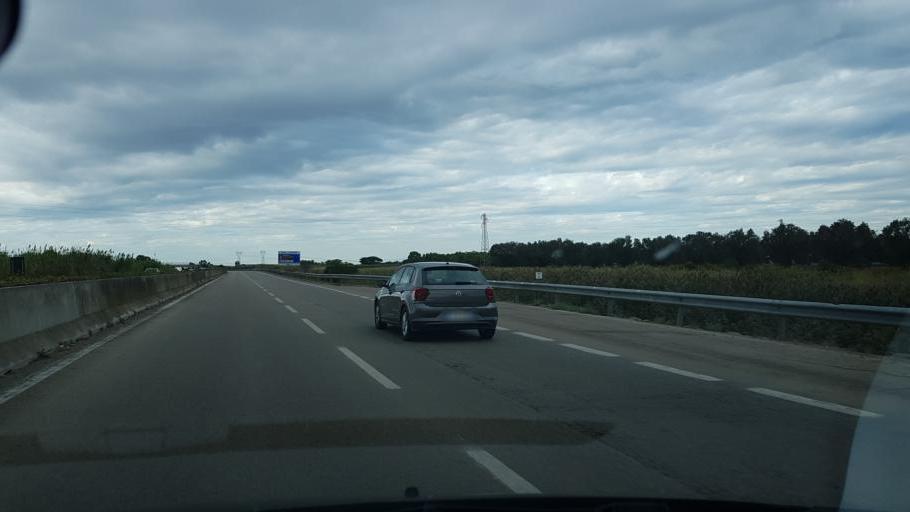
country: IT
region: Apulia
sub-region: Provincia di Brindisi
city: Tuturano
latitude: 40.5467
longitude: 17.9991
